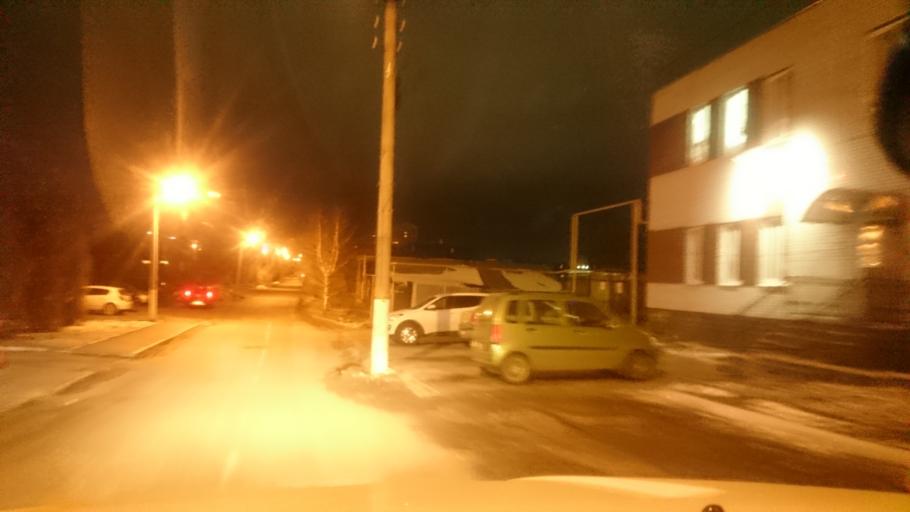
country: RU
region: Tula
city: Tula
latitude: 54.1838
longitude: 37.6298
